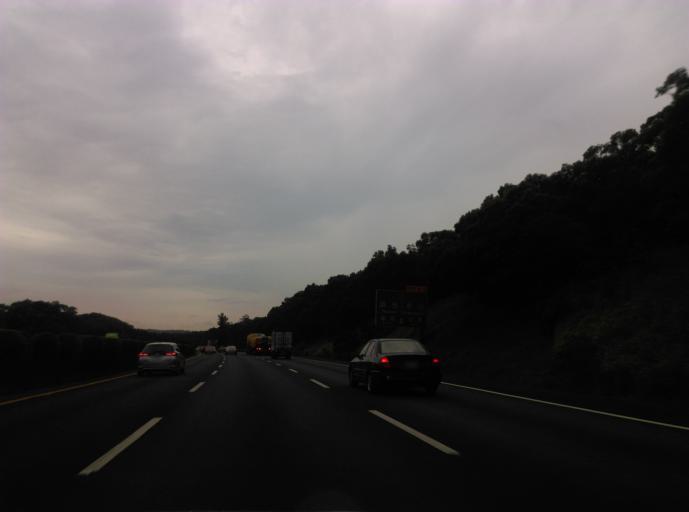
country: TW
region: Taiwan
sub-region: Hsinchu
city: Hsinchu
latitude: 24.7517
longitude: 120.9317
